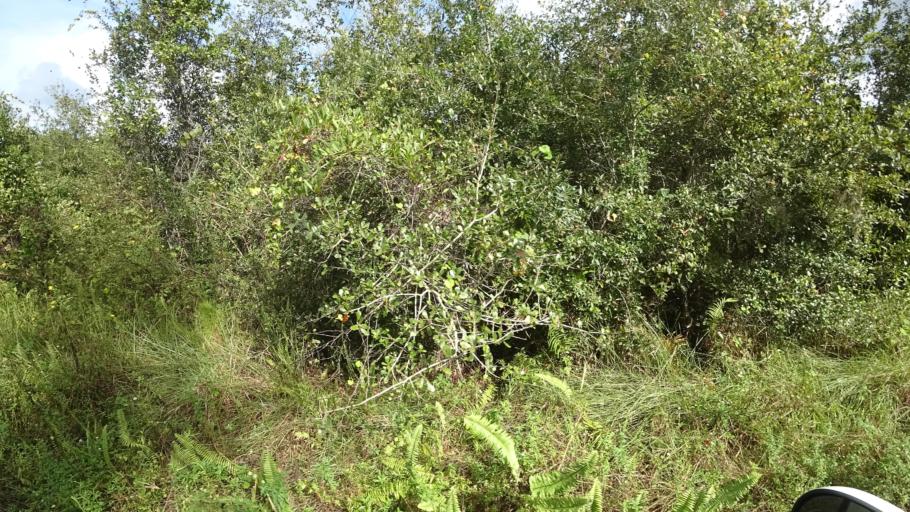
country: US
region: Florida
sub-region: Hillsborough County
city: Wimauma
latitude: 27.5490
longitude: -82.1073
